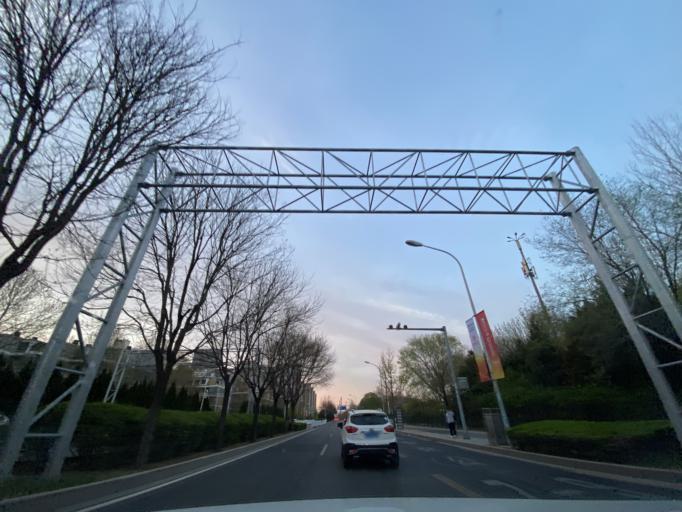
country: CN
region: Beijing
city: Qinghe
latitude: 40.0125
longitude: 116.3687
